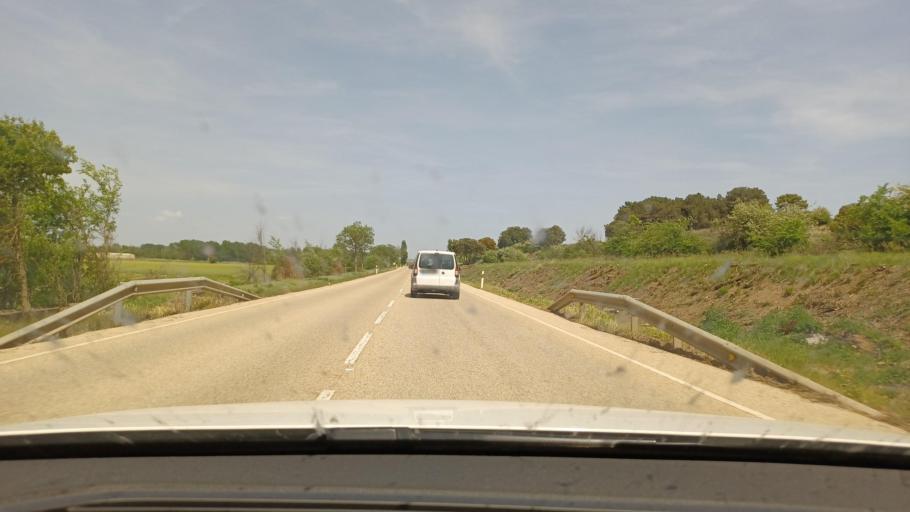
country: ES
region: Castille and Leon
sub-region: Provincia de Soria
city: Almazan
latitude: 41.4720
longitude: -2.5726
